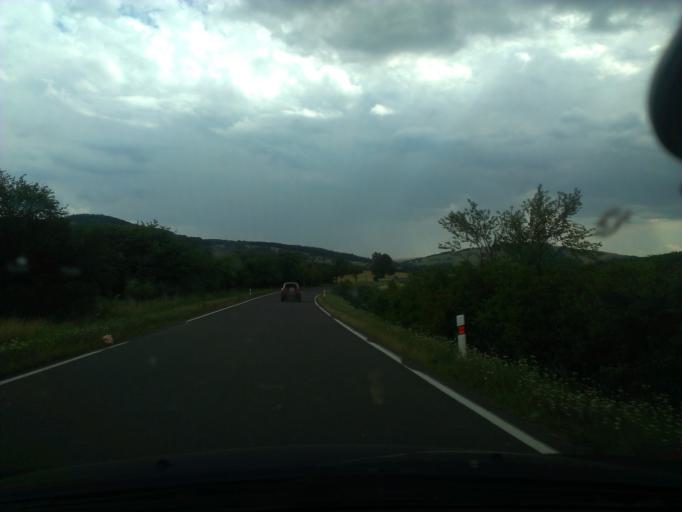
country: CZ
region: South Moravian
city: Velka nad Velickou
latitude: 48.8420
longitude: 17.5199
